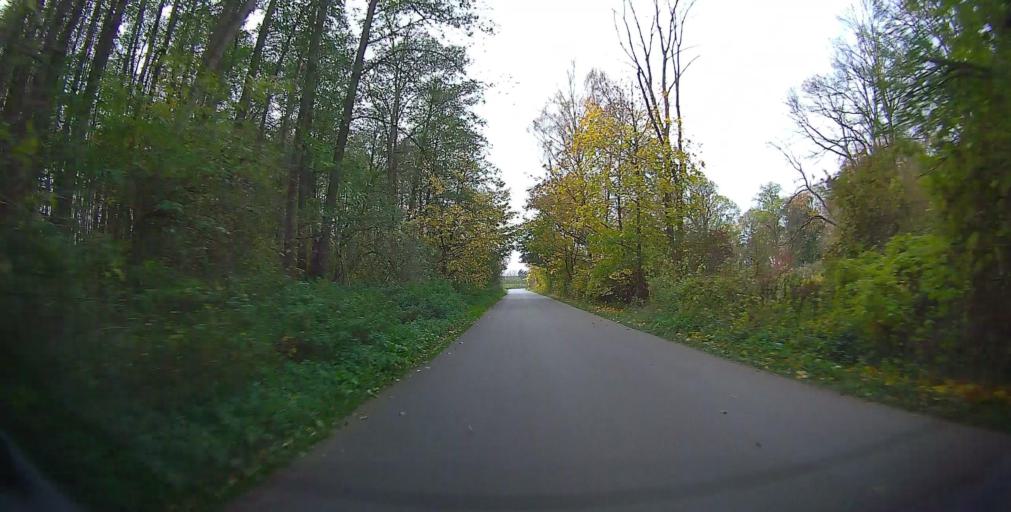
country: PL
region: Masovian Voivodeship
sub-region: Powiat grojecki
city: Mogielnica
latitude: 51.6414
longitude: 20.7498
